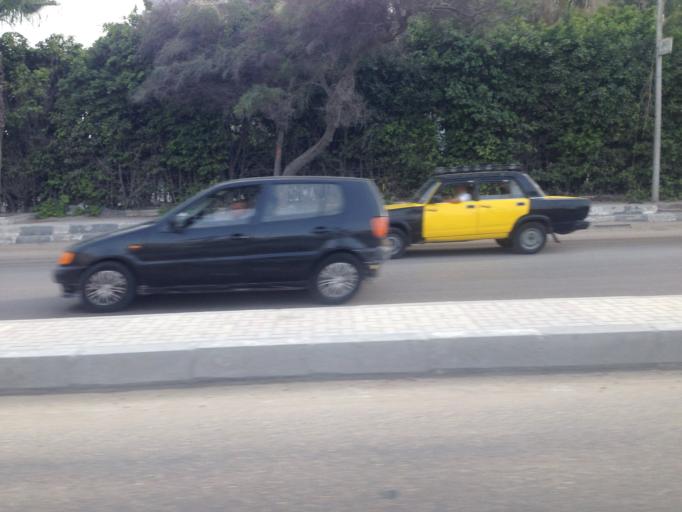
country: EG
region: Alexandria
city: Alexandria
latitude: 31.2088
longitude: 29.9639
